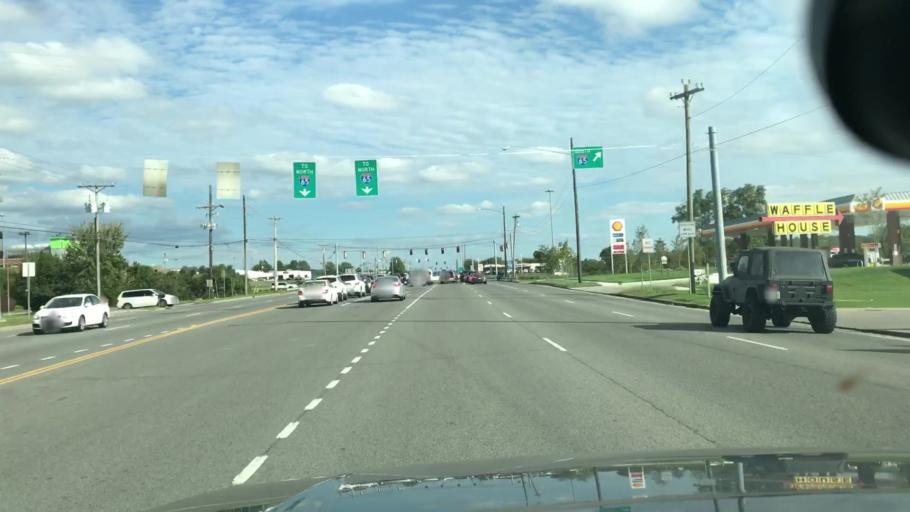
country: US
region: Tennessee
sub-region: Williamson County
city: Franklin
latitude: 35.9148
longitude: -86.8271
